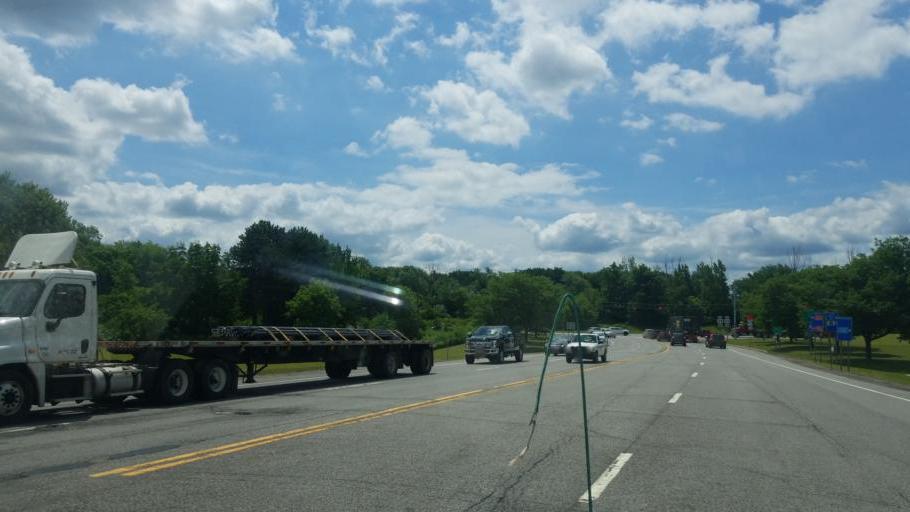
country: US
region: New York
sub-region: Erie County
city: Blasdell
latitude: 42.7910
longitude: -78.8204
